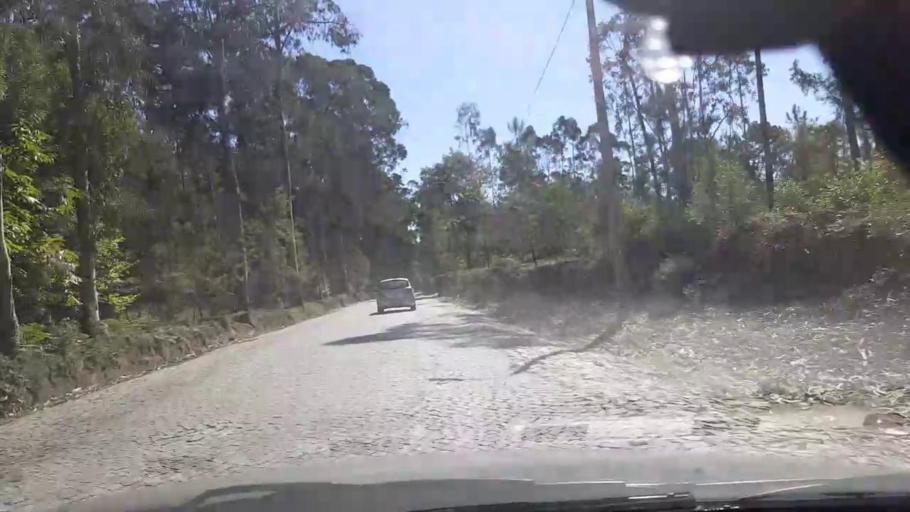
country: PT
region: Porto
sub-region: Vila do Conde
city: Arvore
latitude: 41.3253
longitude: -8.7262
